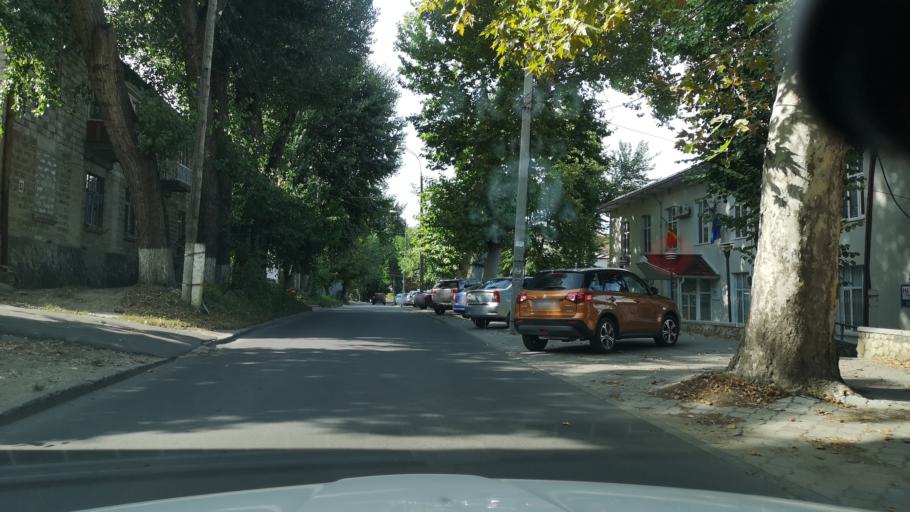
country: MD
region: Chisinau
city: Chisinau
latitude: 47.0343
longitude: 28.8055
